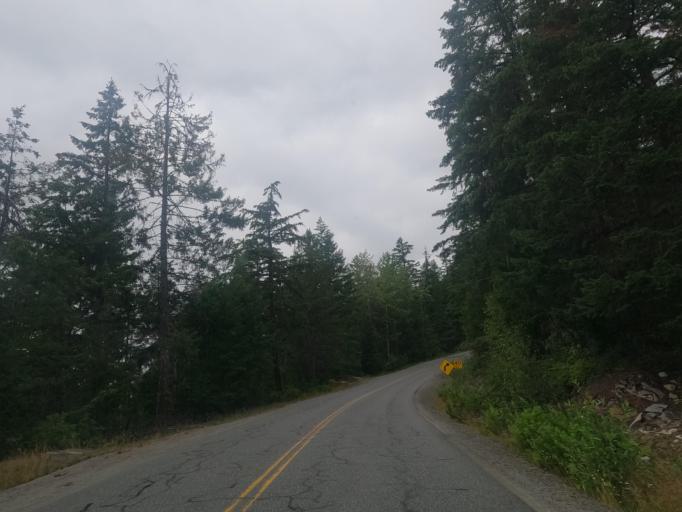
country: CA
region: British Columbia
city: Pemberton
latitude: 50.3055
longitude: -122.5773
